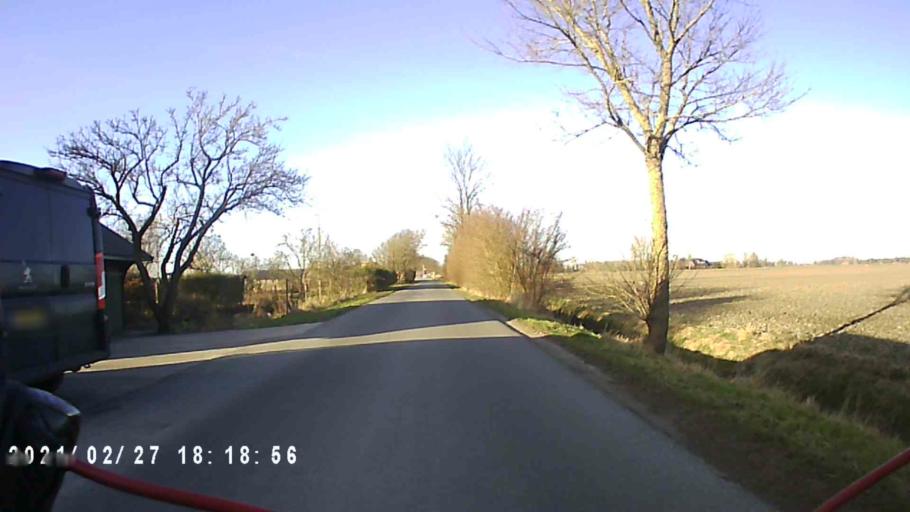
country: NL
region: Groningen
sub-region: Gemeente Bedum
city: Bedum
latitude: 53.3014
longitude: 6.5749
